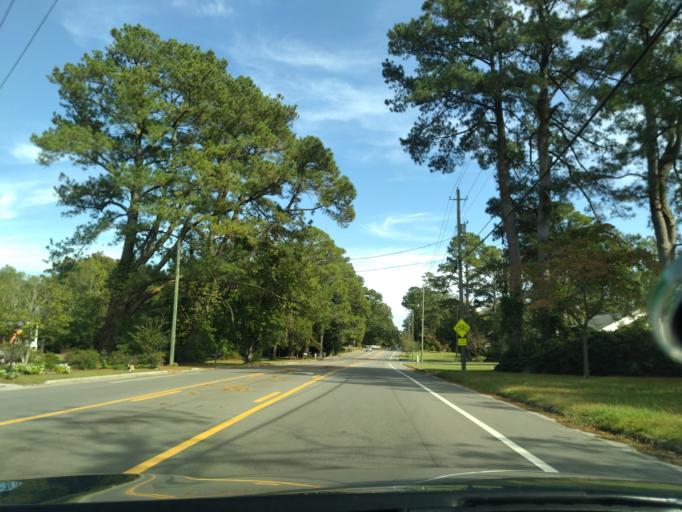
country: US
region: North Carolina
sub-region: Beaufort County
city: Washington
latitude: 35.5343
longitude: -77.0320
